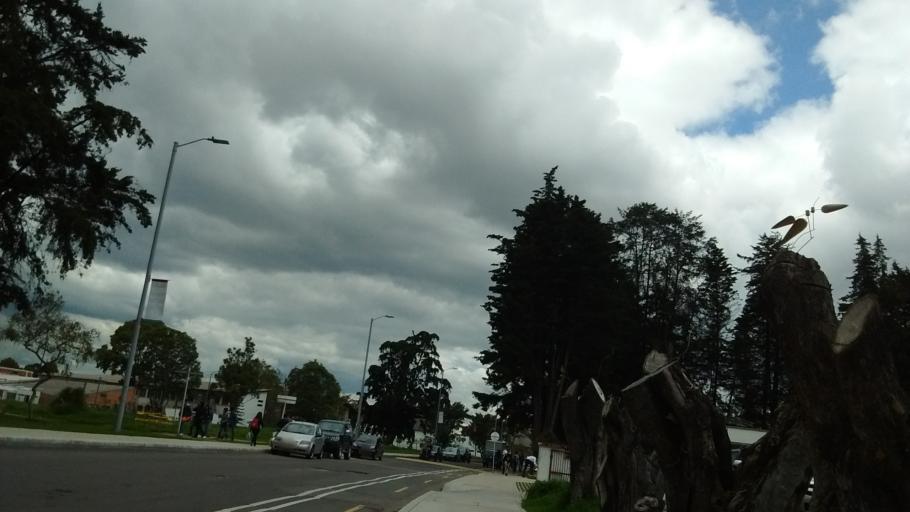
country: CO
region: Bogota D.C.
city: Bogota
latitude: 4.6361
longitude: -74.0864
